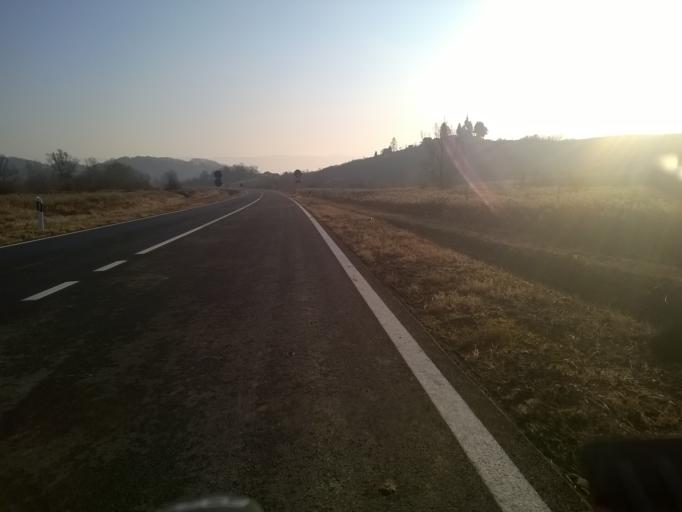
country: HR
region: Krapinsko-Zagorska
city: Zabok
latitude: 46.0437
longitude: 15.9146
